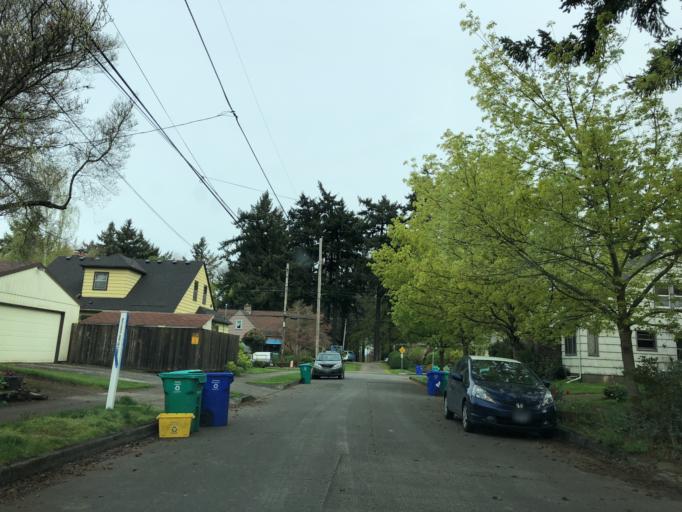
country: US
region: Oregon
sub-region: Multnomah County
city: Portland
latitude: 45.5513
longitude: -122.6277
